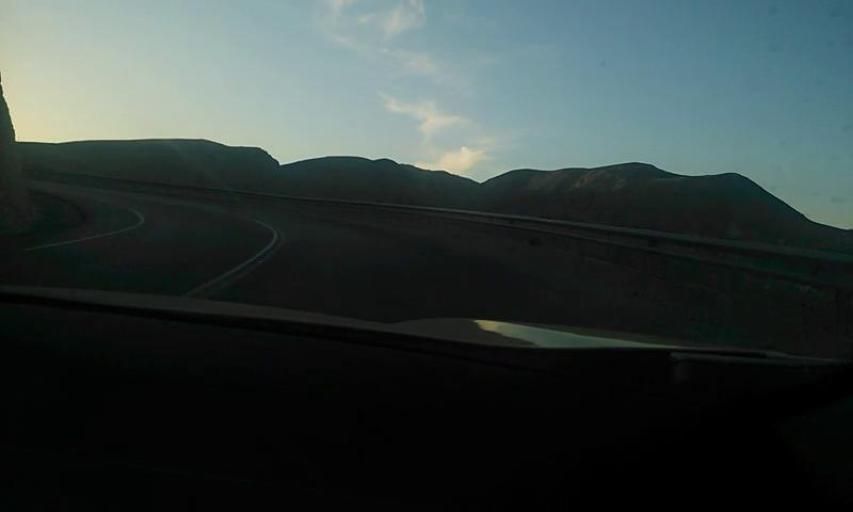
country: PS
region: West Bank
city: An Nuway`imah
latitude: 31.9103
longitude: 35.3745
